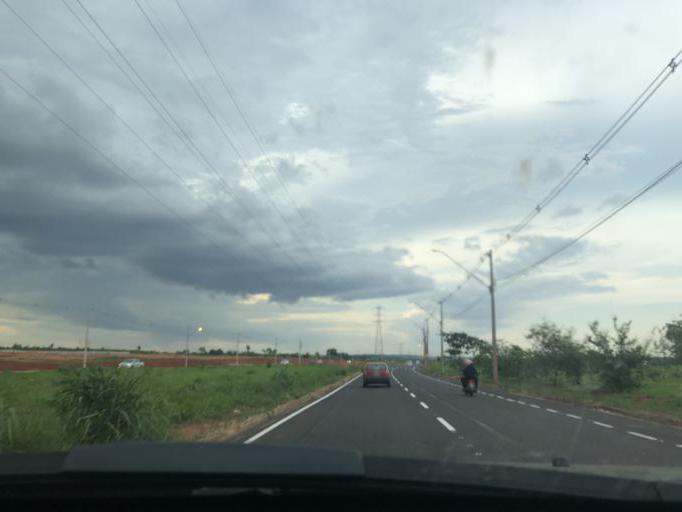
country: BR
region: Sao Paulo
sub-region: Sao Jose Do Rio Preto
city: Sao Jose do Rio Preto
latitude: -20.8372
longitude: -49.4208
